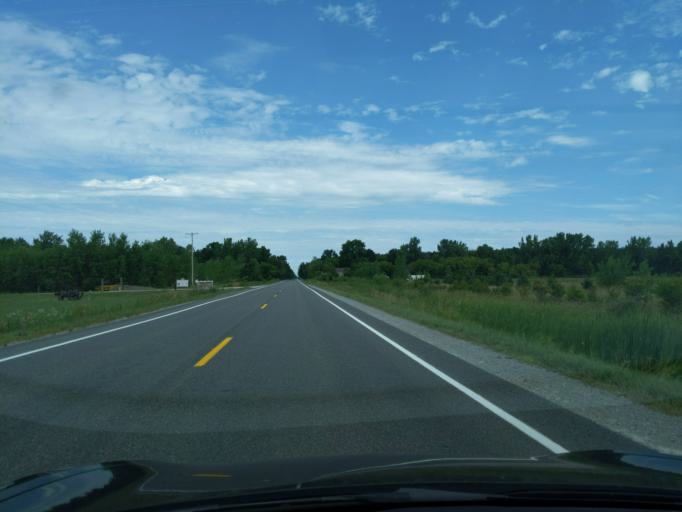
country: US
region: Michigan
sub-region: Gratiot County
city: Breckenridge
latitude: 43.5179
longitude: -84.3698
